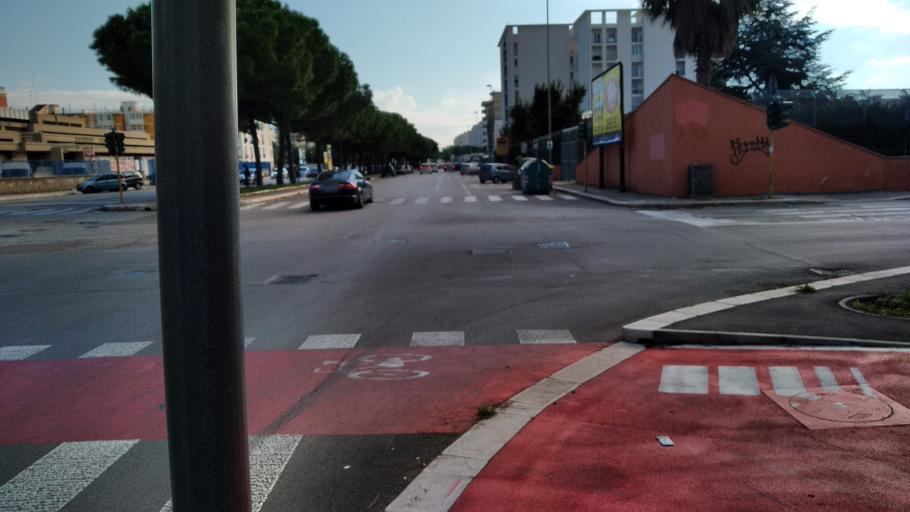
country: IT
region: Apulia
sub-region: Provincia di Bari
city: Bari
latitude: 41.1079
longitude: 16.8952
